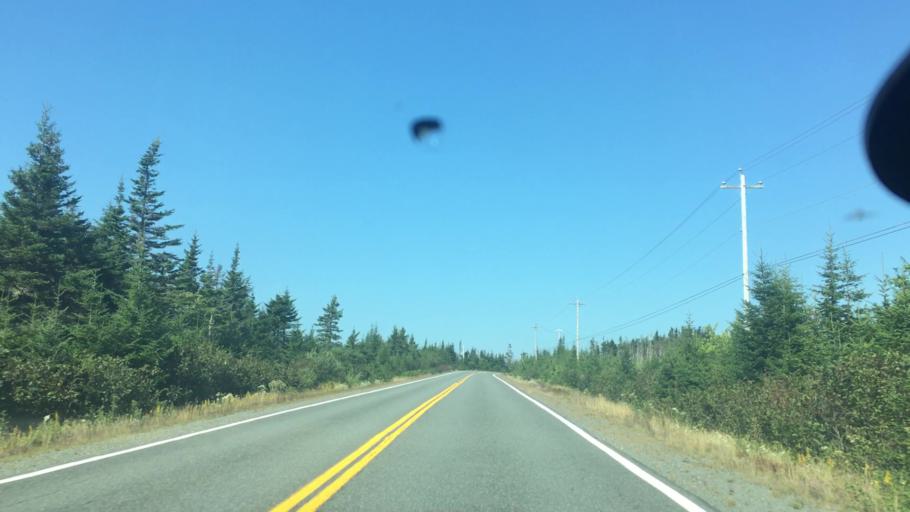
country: CA
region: Nova Scotia
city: Antigonish
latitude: 44.9828
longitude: -62.0941
